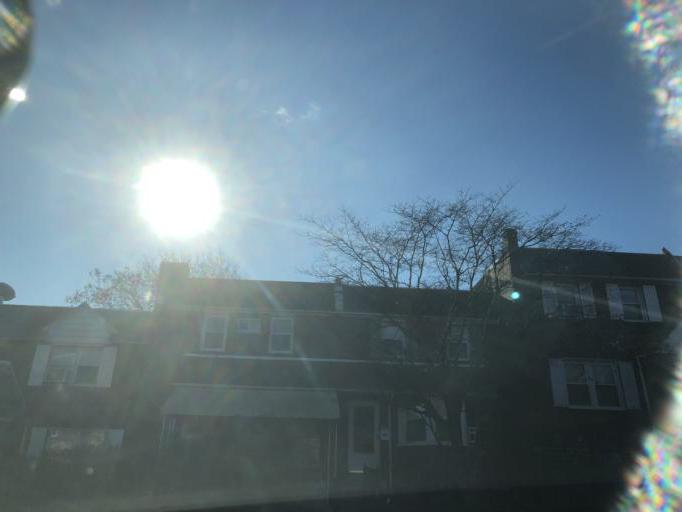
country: US
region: Pennsylvania
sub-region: Delaware County
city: East Lansdowne
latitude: 39.9547
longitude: -75.2623
